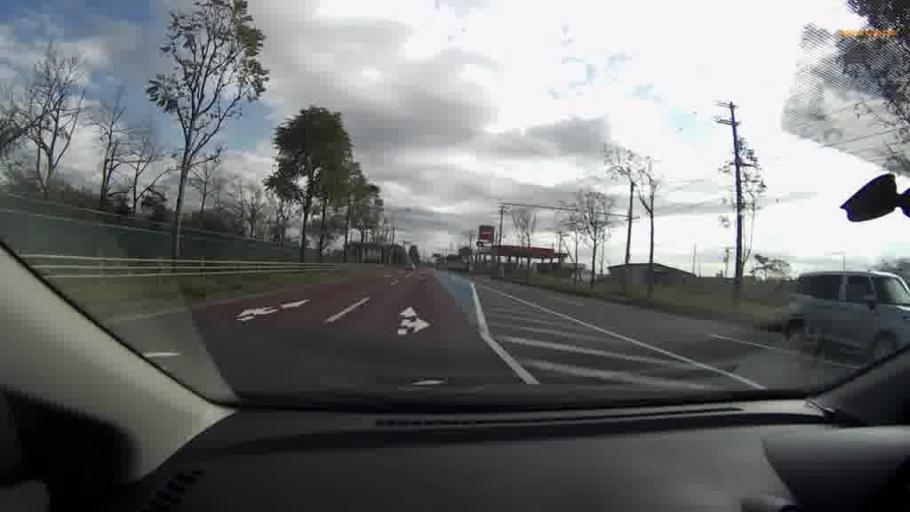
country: JP
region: Hokkaido
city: Kushiro
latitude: 43.0102
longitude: 144.2860
